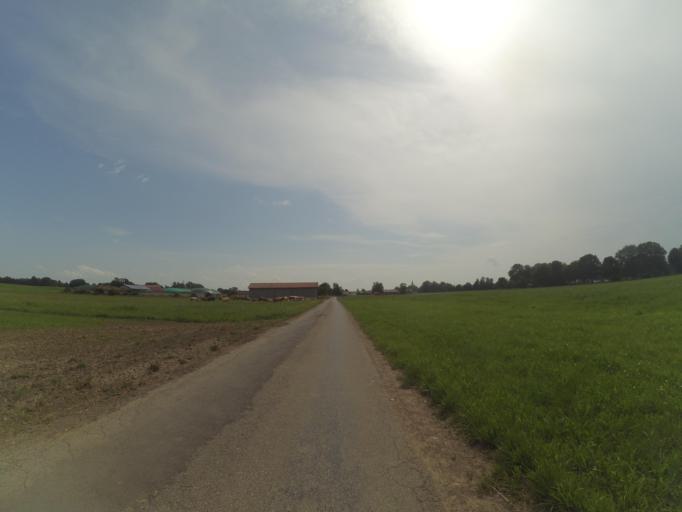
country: DE
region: Bavaria
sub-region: Swabia
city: Jengen
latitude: 48.0077
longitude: 10.7270
